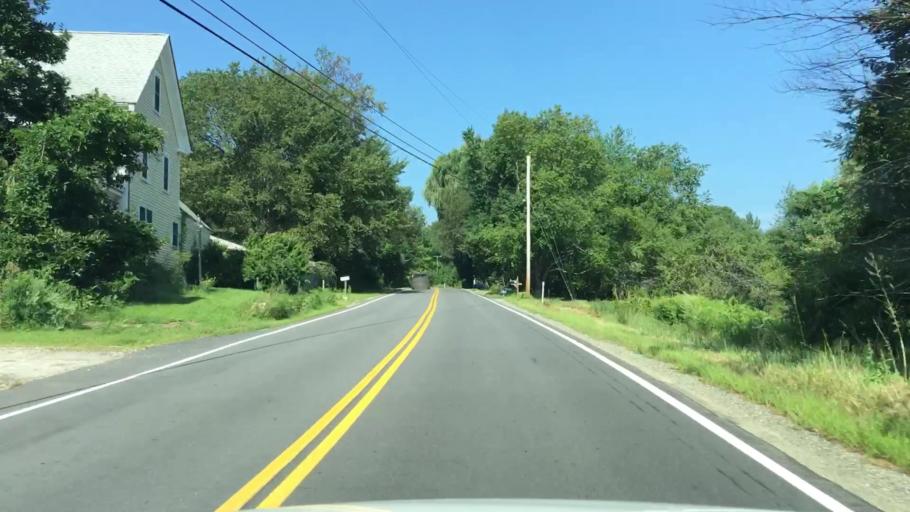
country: US
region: New Hampshire
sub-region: Rockingham County
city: Kensington
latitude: 42.9140
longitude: -70.9666
